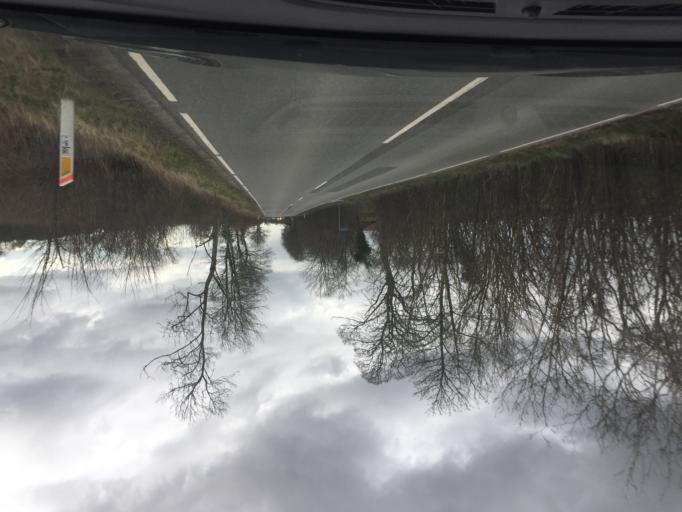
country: DK
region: South Denmark
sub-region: Kerteminde Kommune
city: Langeskov
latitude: 55.3008
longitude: 10.5966
